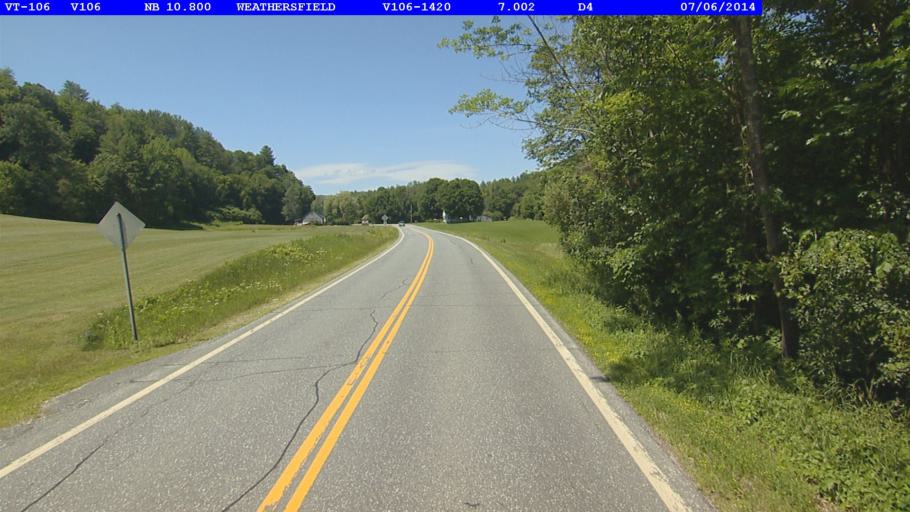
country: US
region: Vermont
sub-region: Windsor County
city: Springfield
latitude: 43.4357
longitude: -72.5291
